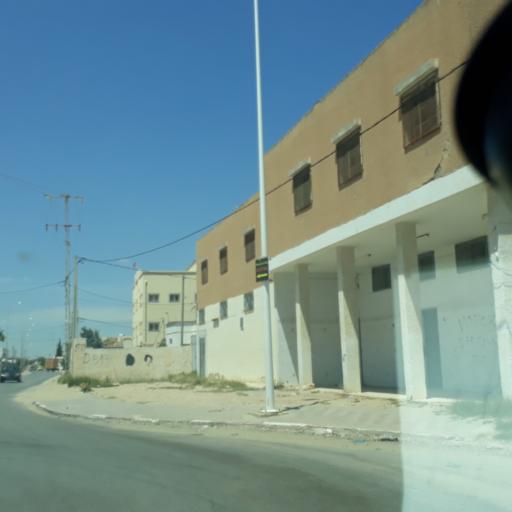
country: TN
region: Safaqis
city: Al Qarmadah
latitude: 34.8170
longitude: 10.7443
